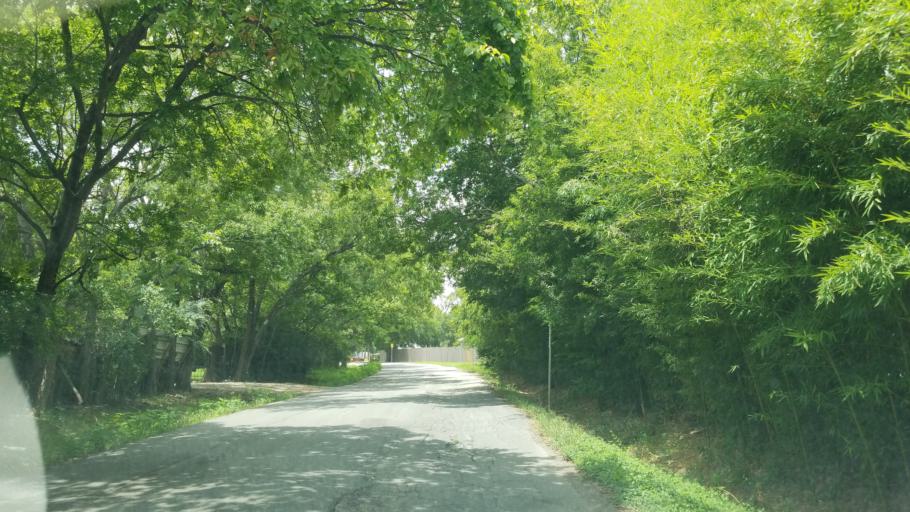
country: US
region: Texas
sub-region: Dallas County
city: Cockrell Hill
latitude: 32.7889
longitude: -96.8989
